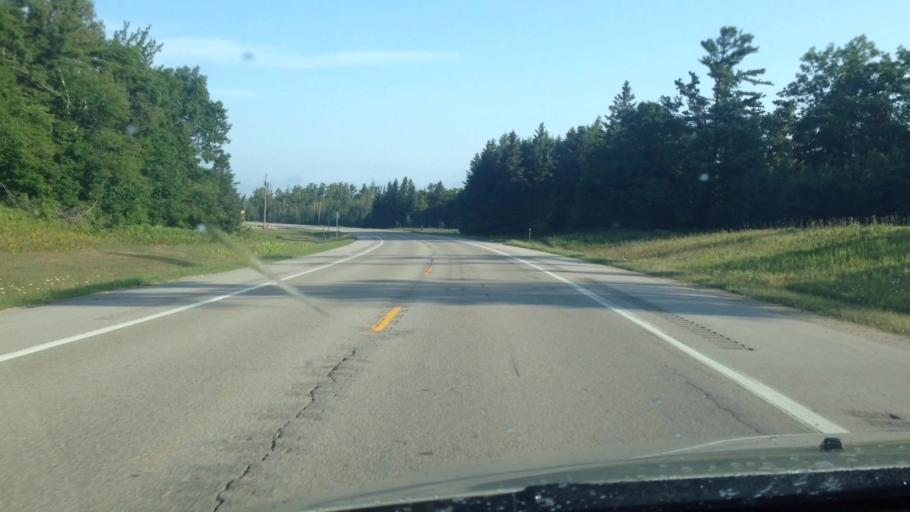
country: US
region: Michigan
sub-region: Mackinac County
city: Saint Ignace
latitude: 45.8946
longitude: -84.8329
